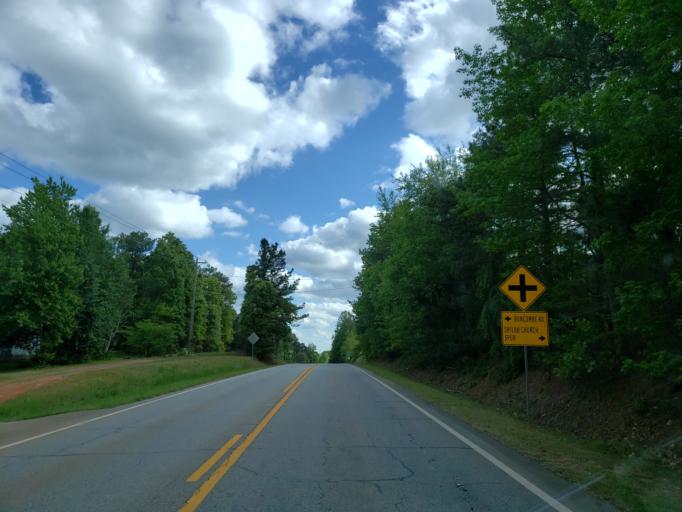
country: US
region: Georgia
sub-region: Carroll County
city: Mount Zion
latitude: 33.6600
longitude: -85.2681
